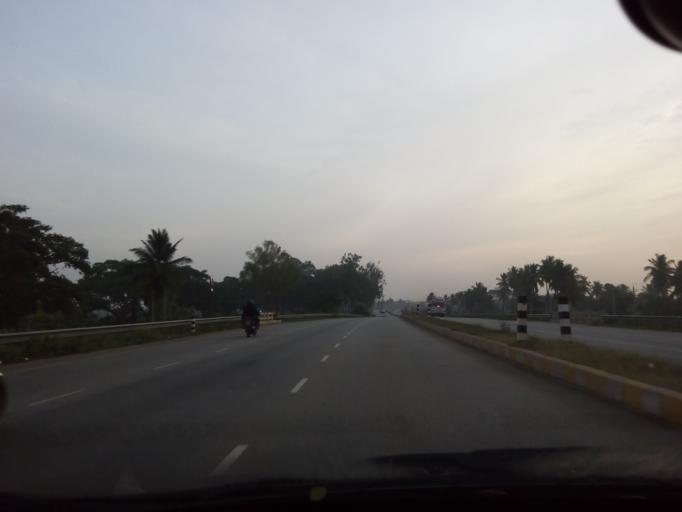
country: IN
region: Karnataka
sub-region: Bangalore Rural
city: Devanhalli
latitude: 13.2467
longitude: 77.7060
